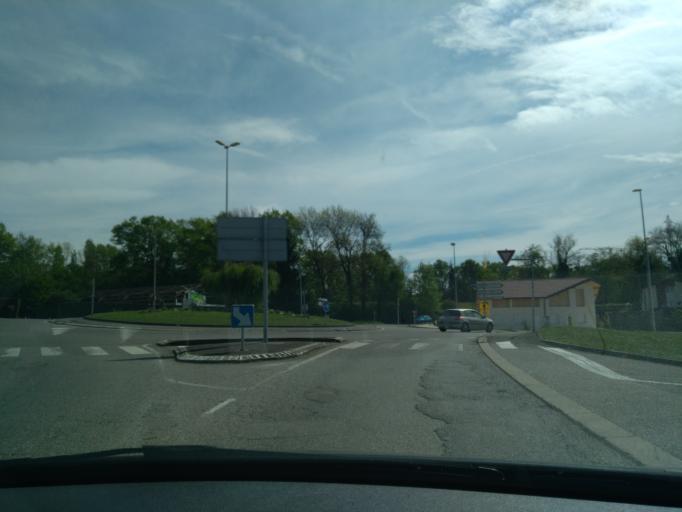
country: FR
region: Rhone-Alpes
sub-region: Departement de la Haute-Savoie
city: Seynod
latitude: 45.8912
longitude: 6.0870
